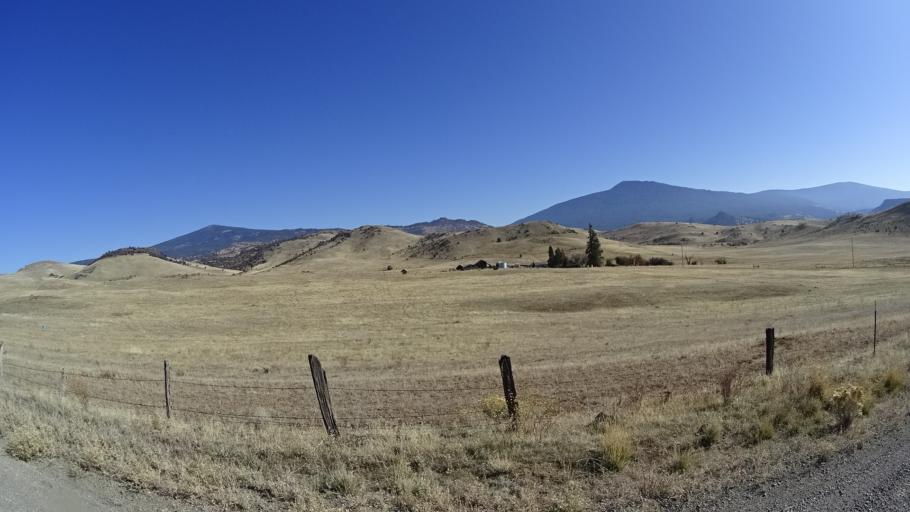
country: US
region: California
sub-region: Siskiyou County
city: Montague
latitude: 41.7654
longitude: -122.3569
